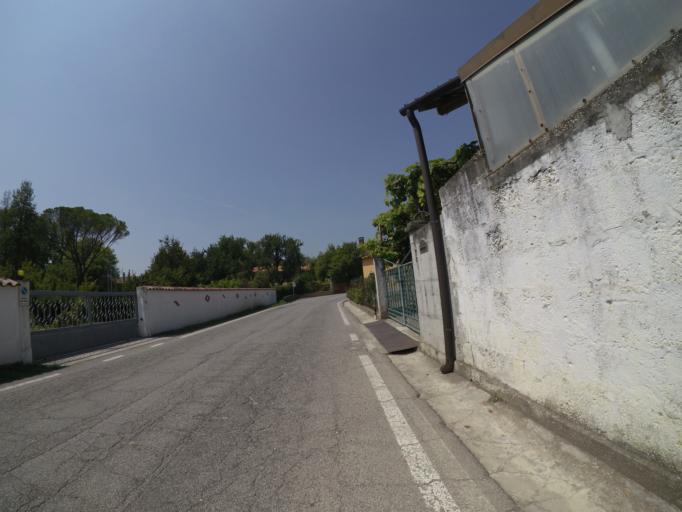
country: IT
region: Friuli Venezia Giulia
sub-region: Provincia di Udine
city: Varmo
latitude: 45.8989
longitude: 12.9641
